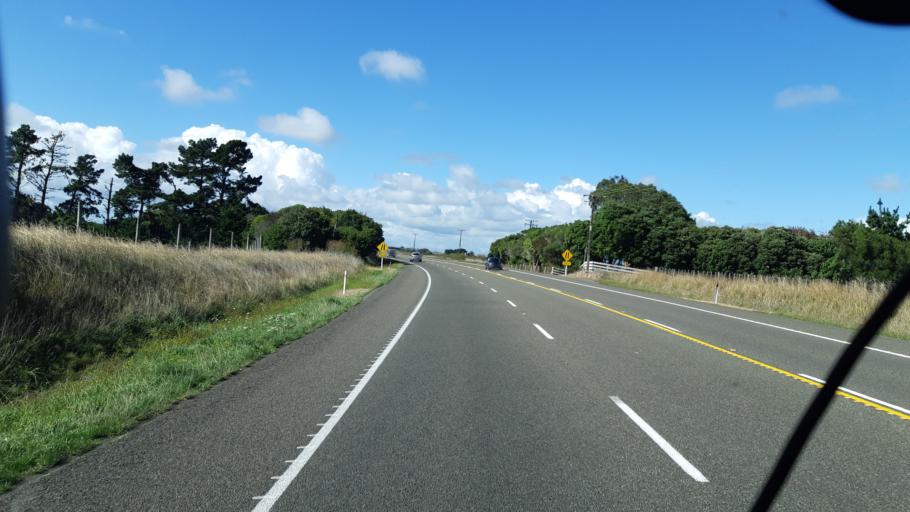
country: NZ
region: Manawatu-Wanganui
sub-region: Wanganui District
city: Wanganui
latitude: -39.9744
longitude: 175.1179
